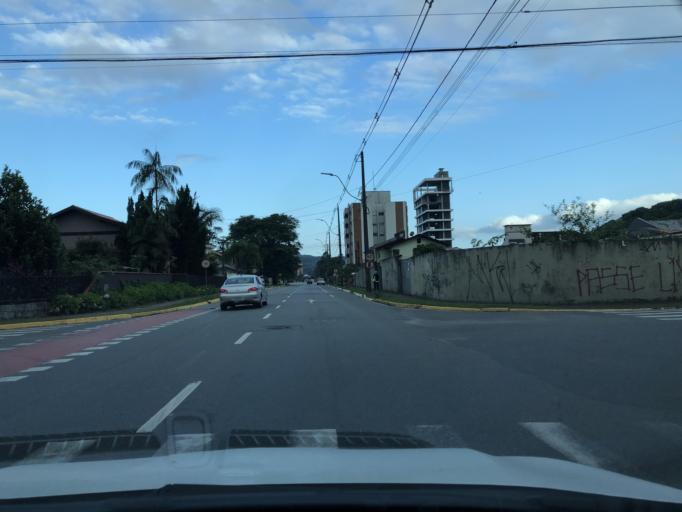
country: BR
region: Santa Catarina
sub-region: Joinville
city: Joinville
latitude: -26.2929
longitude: -48.8620
